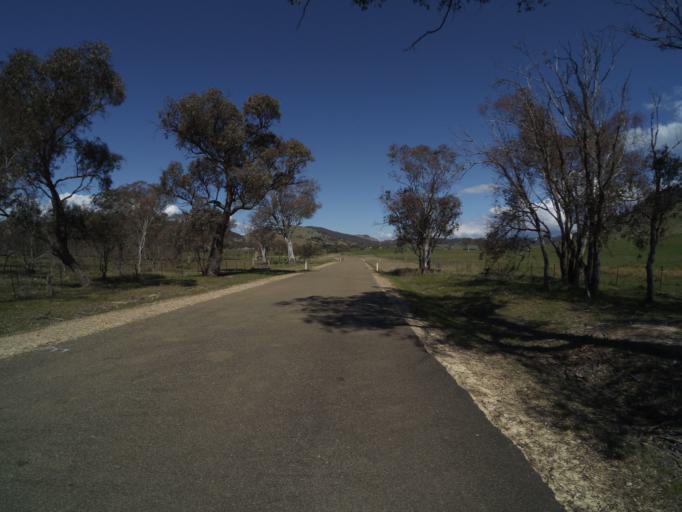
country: AU
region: Australian Capital Territory
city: Macquarie
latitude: -35.1413
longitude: 148.8774
